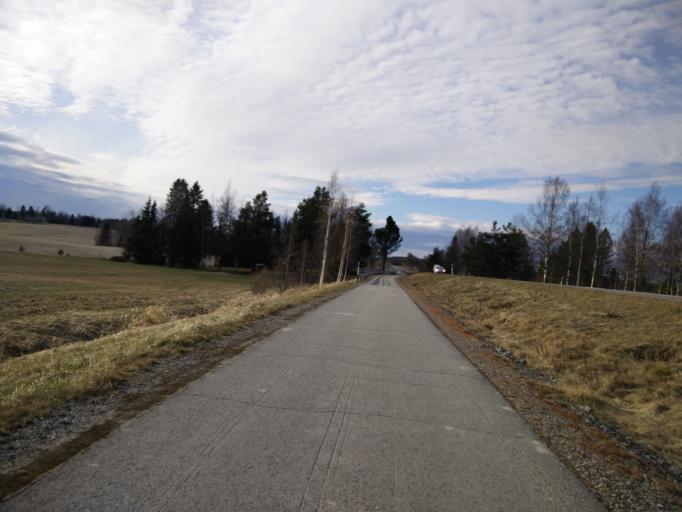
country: FI
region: Pirkanmaa
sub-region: Tampere
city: Orivesi
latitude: 61.7049
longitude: 24.3372
